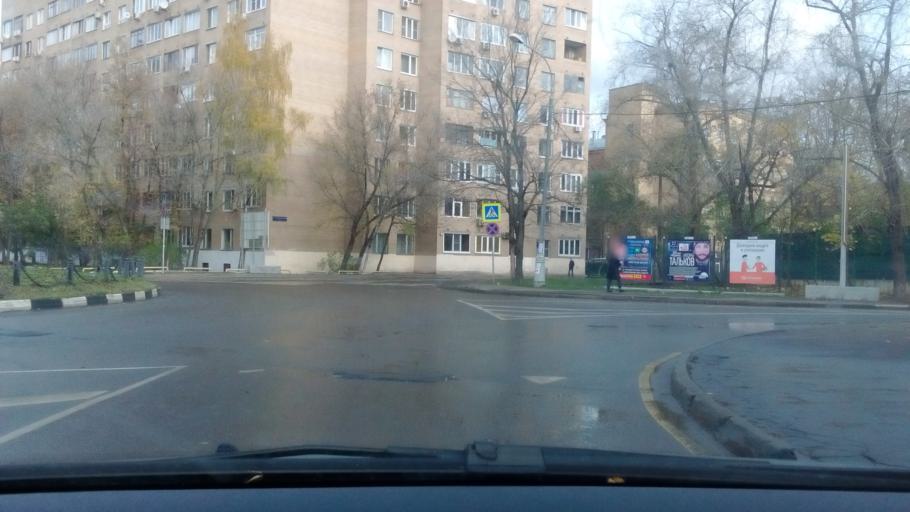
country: RU
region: Moscow
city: Sokol
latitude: 55.7976
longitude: 37.5537
